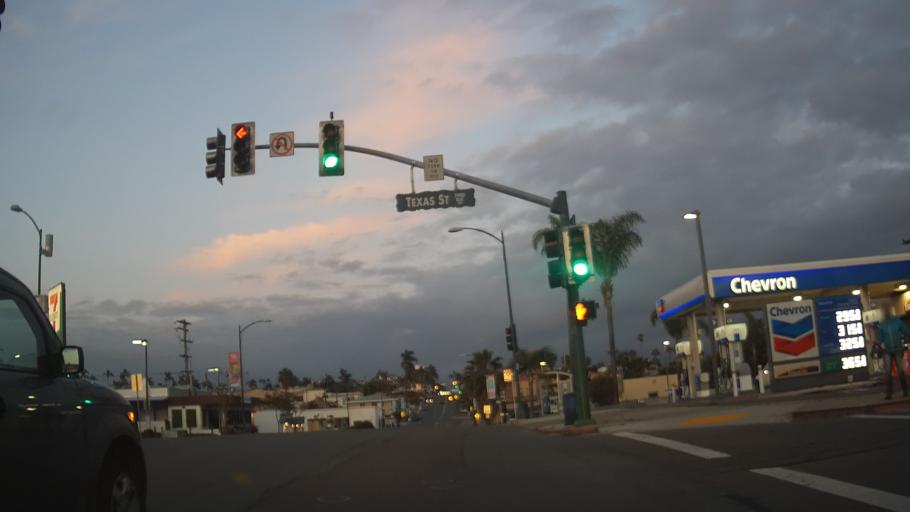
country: US
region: California
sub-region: San Diego County
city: San Diego
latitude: 32.7484
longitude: -117.1391
